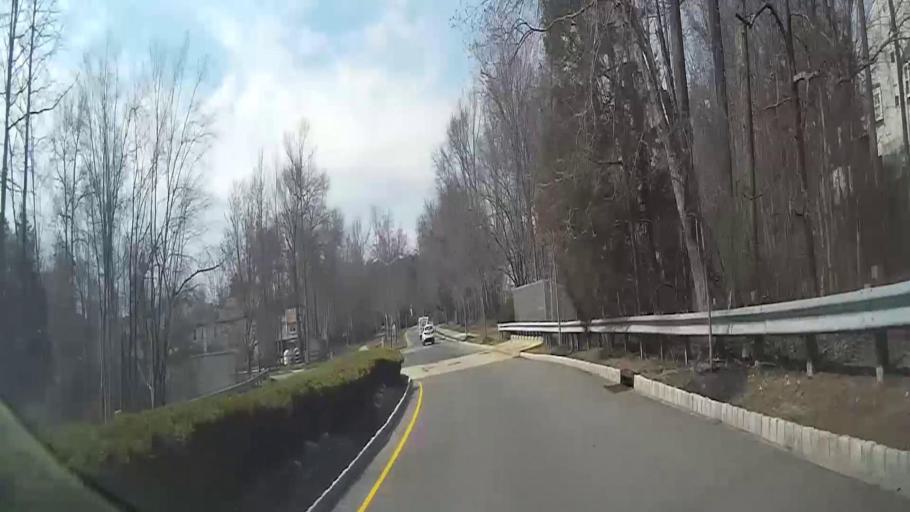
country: US
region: New Jersey
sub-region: Burlington County
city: Marlton
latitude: 39.8717
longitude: -74.8648
